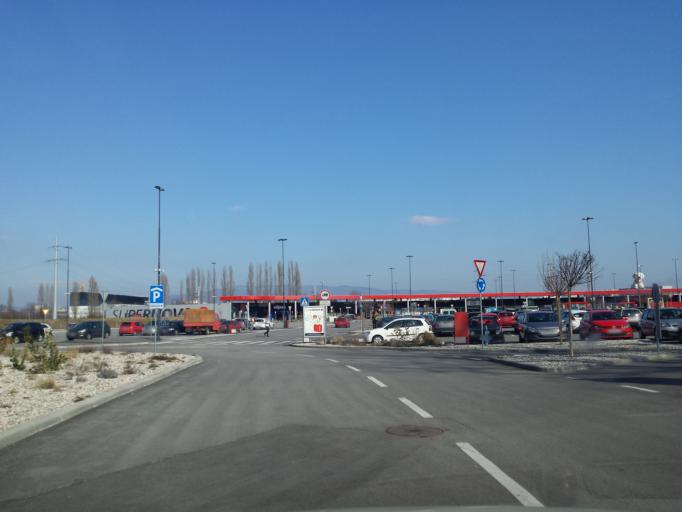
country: HR
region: Grad Zagreb
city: Odra
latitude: 45.7547
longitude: 15.9869
